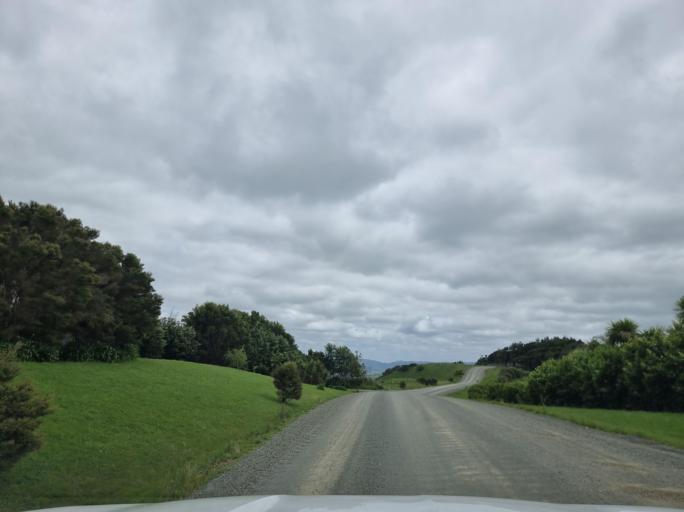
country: NZ
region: Auckland
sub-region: Auckland
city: Wellsford
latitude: -36.1692
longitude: 174.5545
